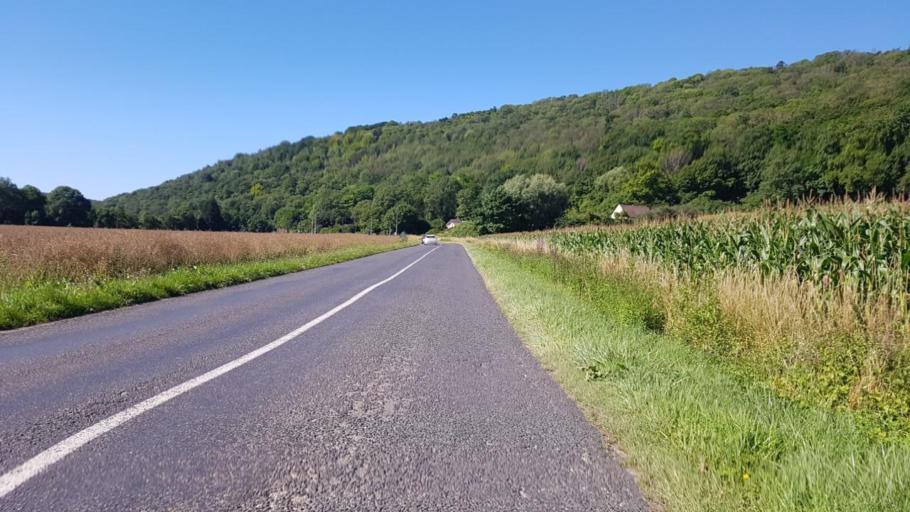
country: FR
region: Picardie
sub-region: Departement de l'Aisne
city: Chezy-sur-Marne
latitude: 49.0021
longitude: 3.3436
